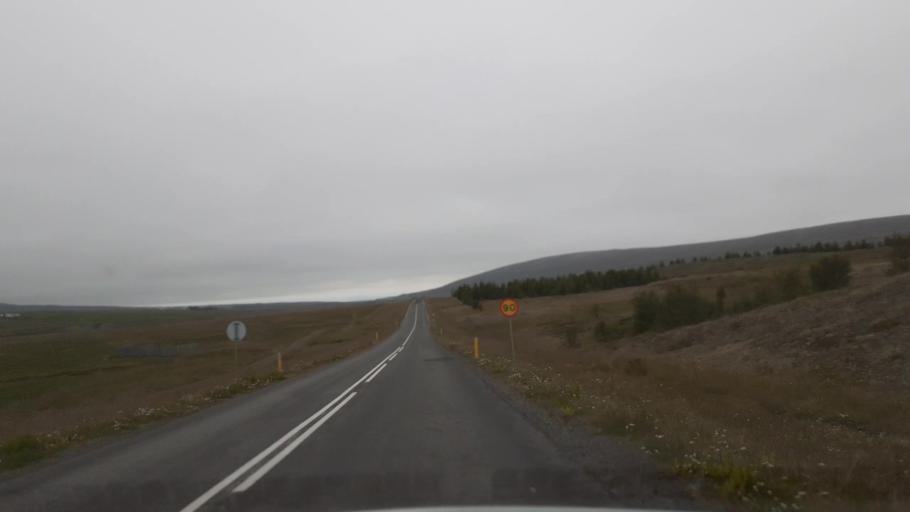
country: IS
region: Northeast
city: Siglufjoerdur
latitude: 65.7373
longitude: -19.1298
